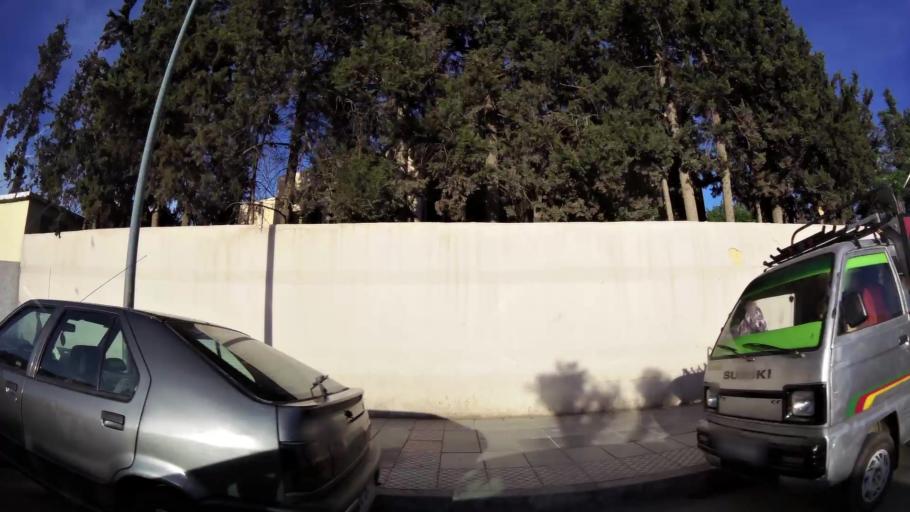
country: MA
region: Oriental
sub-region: Oujda-Angad
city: Oujda
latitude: 34.6781
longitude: -1.9081
